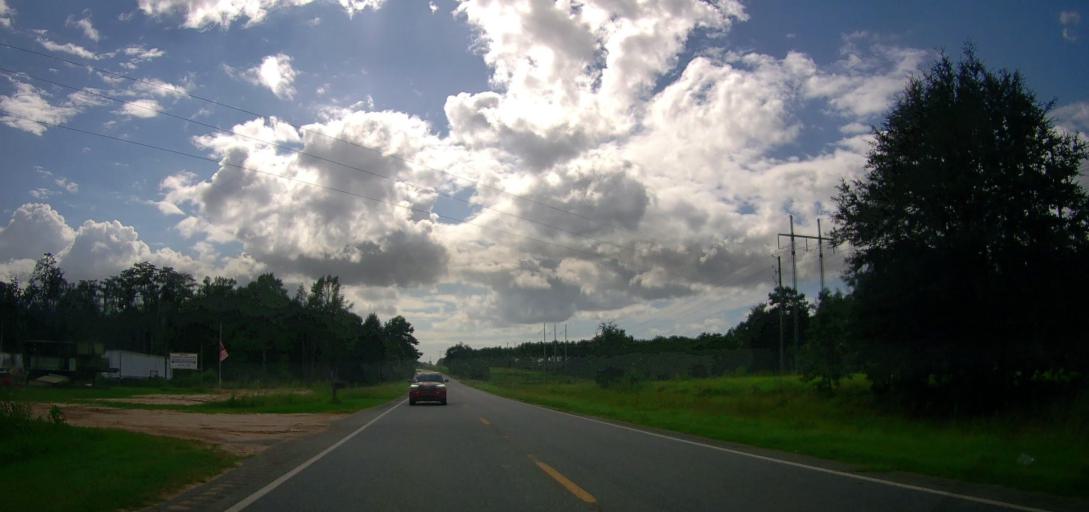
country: US
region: Georgia
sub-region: Coffee County
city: Douglas
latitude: 31.5386
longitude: -82.8232
